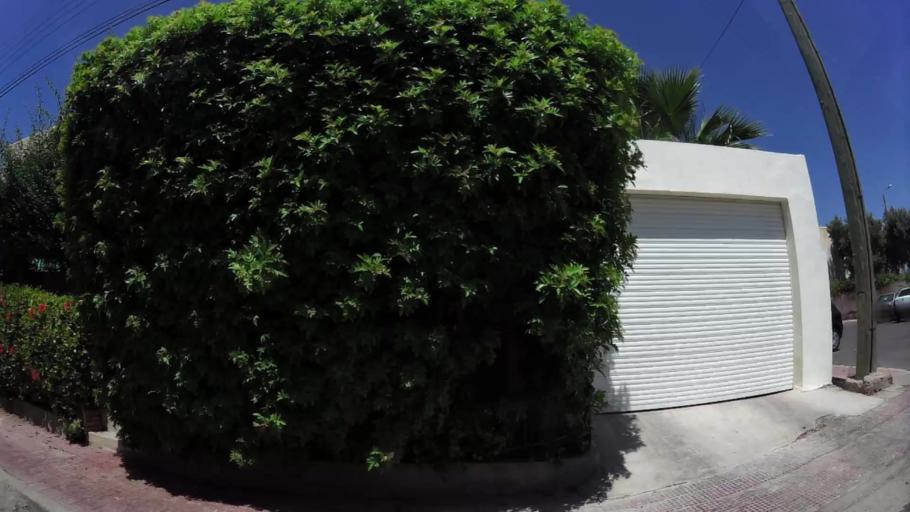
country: MA
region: Souss-Massa-Draa
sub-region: Agadir-Ida-ou-Tnan
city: Agadir
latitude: 30.4312
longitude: -9.5896
